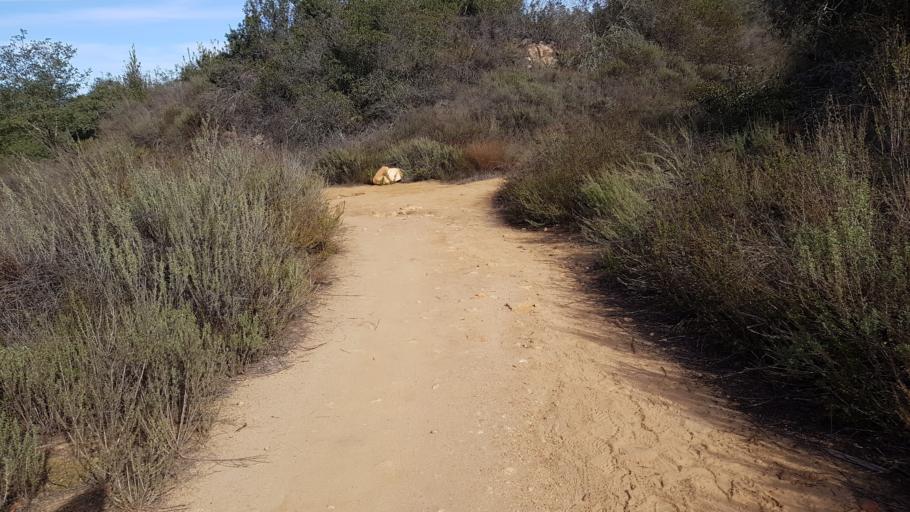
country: US
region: California
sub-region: San Diego County
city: Valley Center
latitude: 33.1787
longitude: -117.0374
